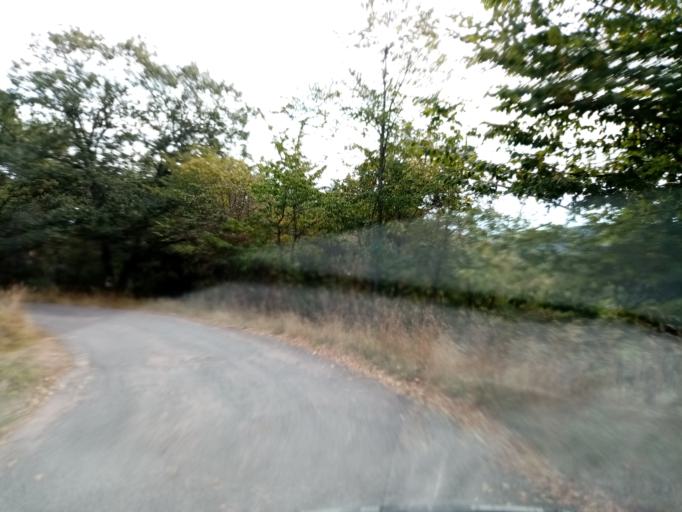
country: FR
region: Alsace
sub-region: Departement du Bas-Rhin
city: Andlau
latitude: 48.3530
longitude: 7.3731
